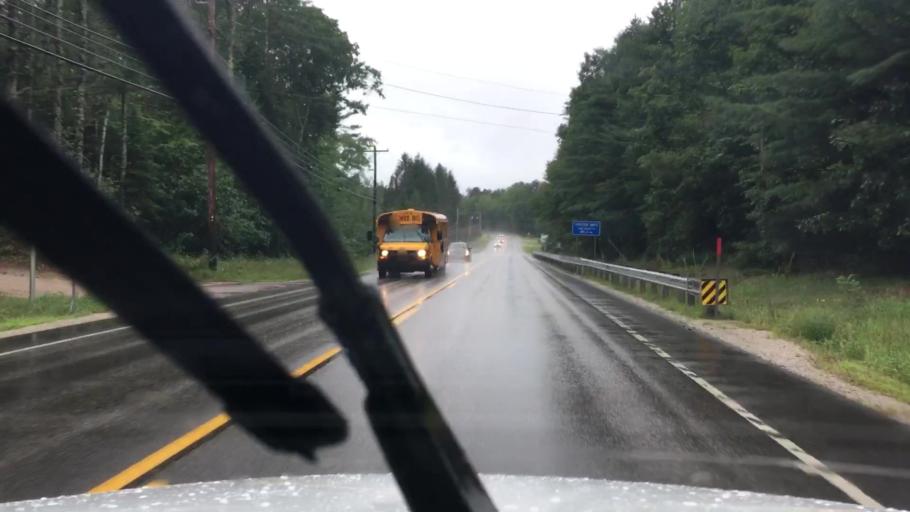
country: US
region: Maine
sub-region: Oxford County
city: Fryeburg
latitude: 43.9980
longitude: -71.0198
